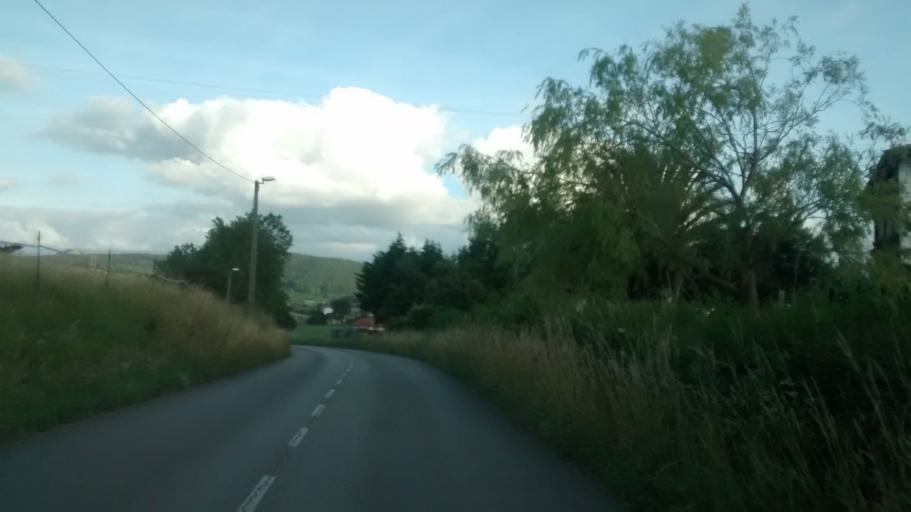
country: ES
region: Cantabria
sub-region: Provincia de Cantabria
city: Lierganes
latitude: 43.4071
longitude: -3.7420
